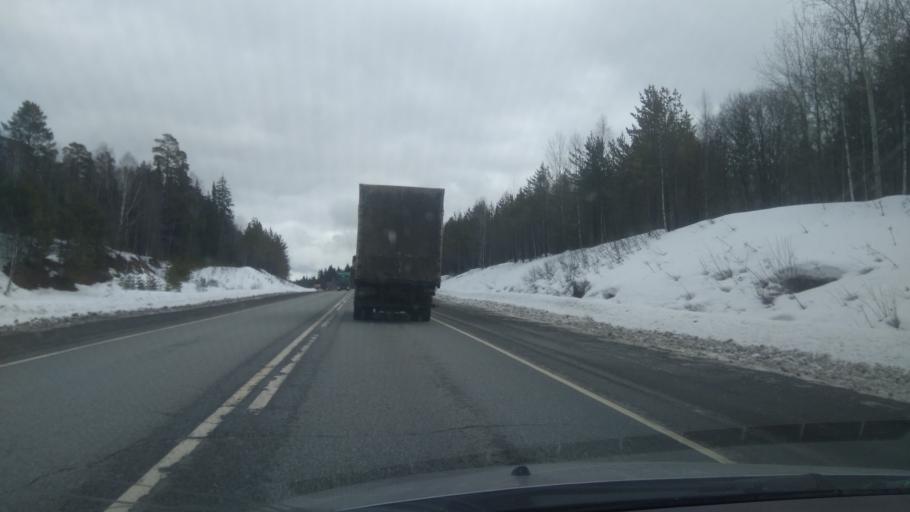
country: RU
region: Sverdlovsk
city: Atig
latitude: 56.8007
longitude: 59.3837
